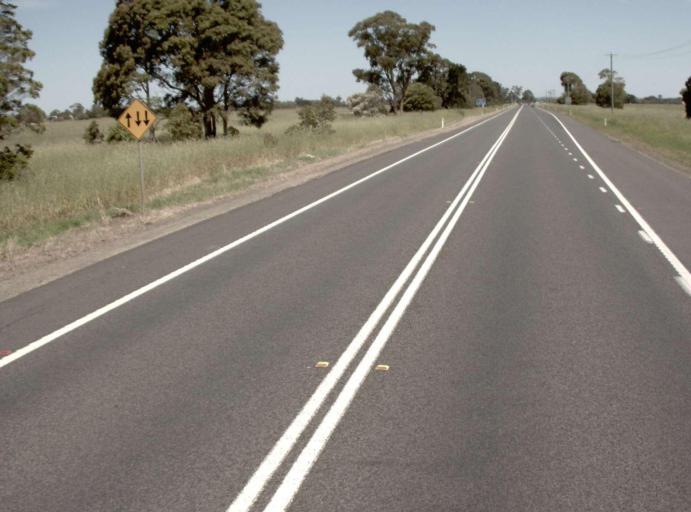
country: AU
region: Victoria
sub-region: Wellington
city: Sale
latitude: -38.0586
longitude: 147.0697
